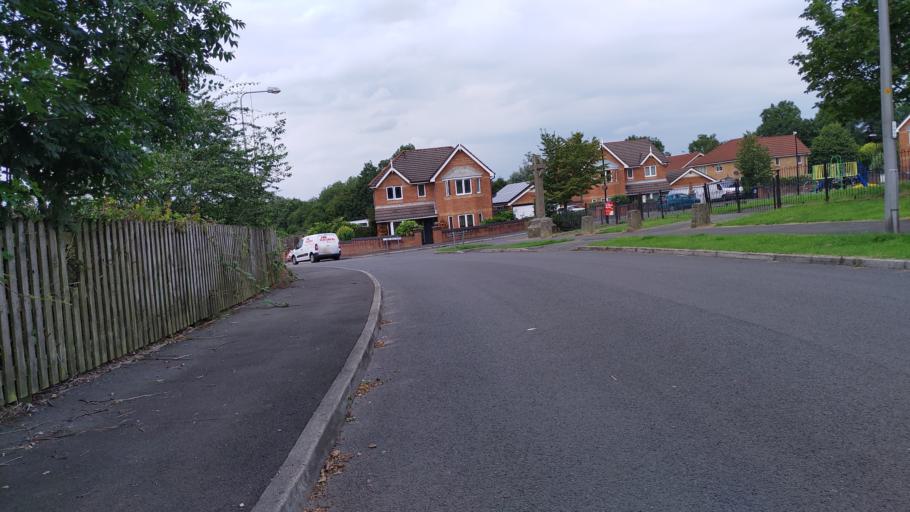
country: GB
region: England
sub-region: Lancashire
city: Coppull
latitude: 53.6338
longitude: -2.6383
